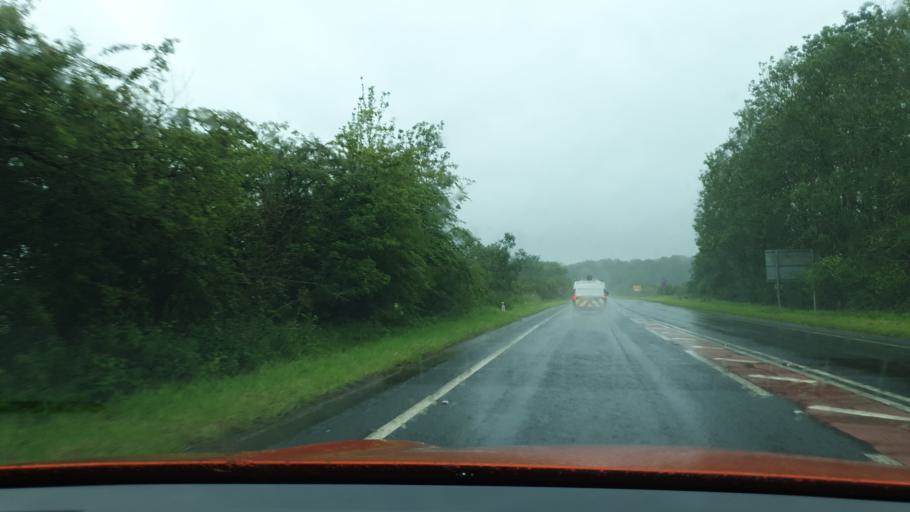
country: GB
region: England
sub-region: Cumbria
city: Arnside
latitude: 54.2472
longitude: -2.8435
